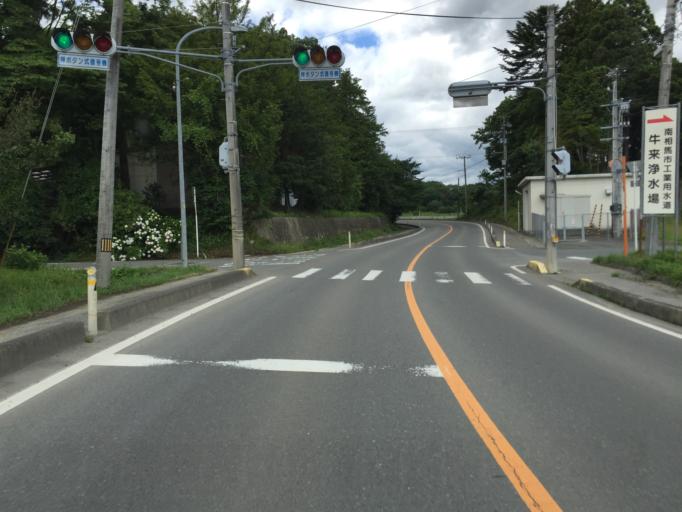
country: JP
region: Fukushima
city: Namie
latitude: 37.6209
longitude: 140.9694
